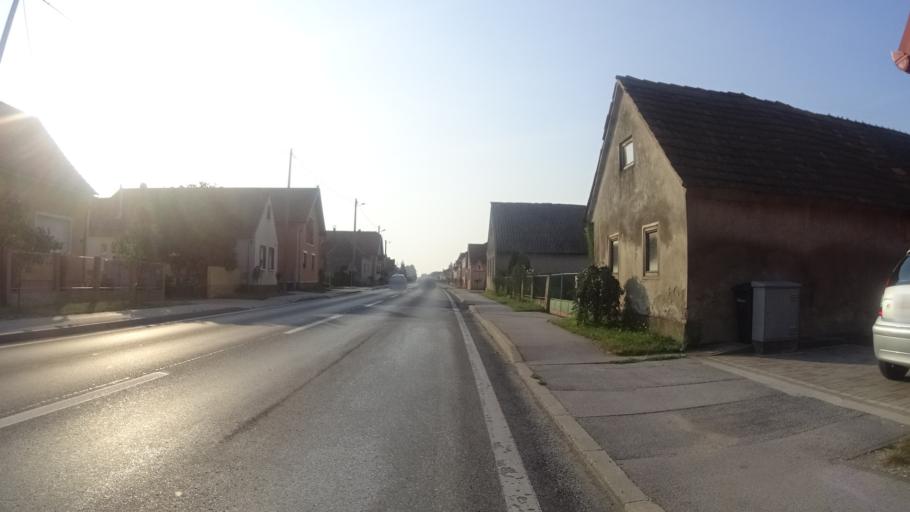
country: HR
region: Varazdinska
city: Sracinec
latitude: 46.3310
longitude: 16.2752
